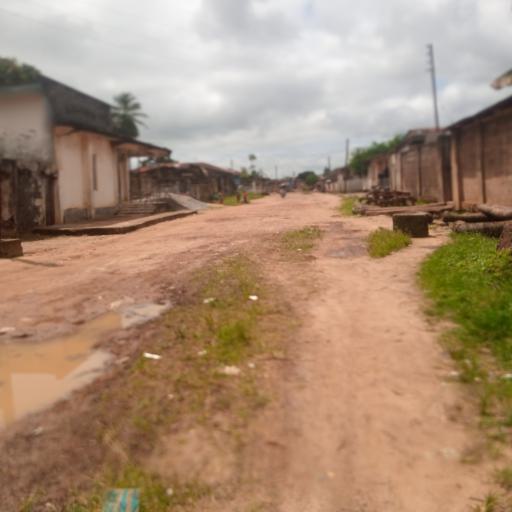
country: SL
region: Eastern Province
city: Kenema
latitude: 7.8891
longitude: -11.1867
